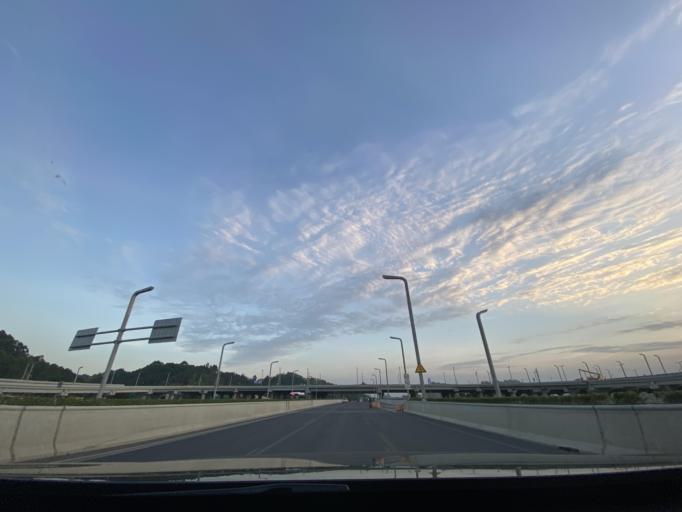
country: CN
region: Sichuan
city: Longquan
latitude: 30.5959
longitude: 104.3062
